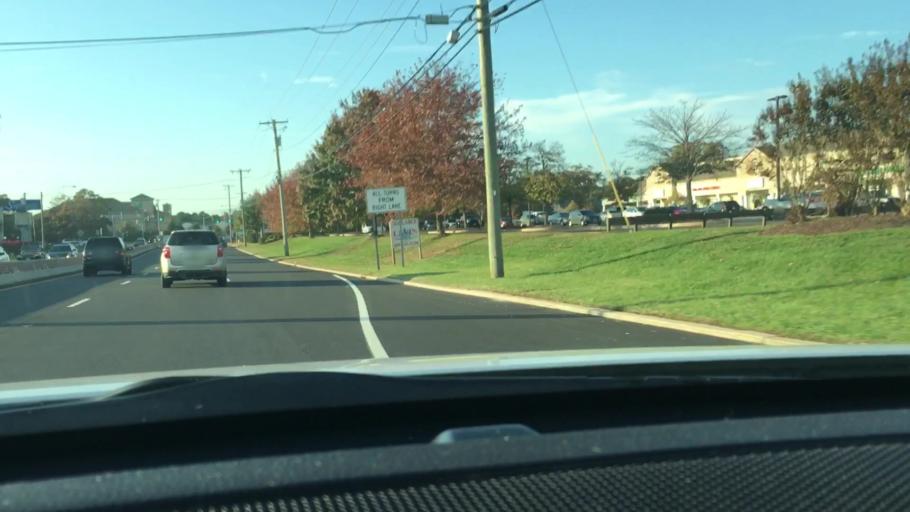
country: US
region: New Jersey
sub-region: Atlantic County
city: Absecon
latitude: 39.4344
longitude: -74.5144
